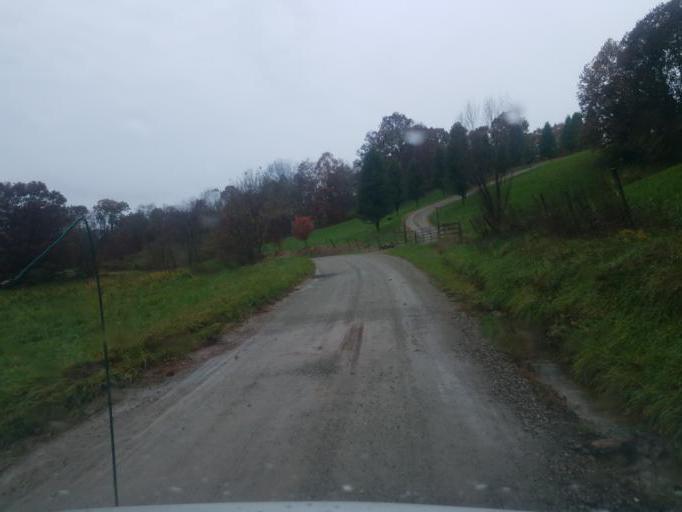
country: US
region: Ohio
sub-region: Washington County
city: Beverly
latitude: 39.4699
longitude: -81.6816
